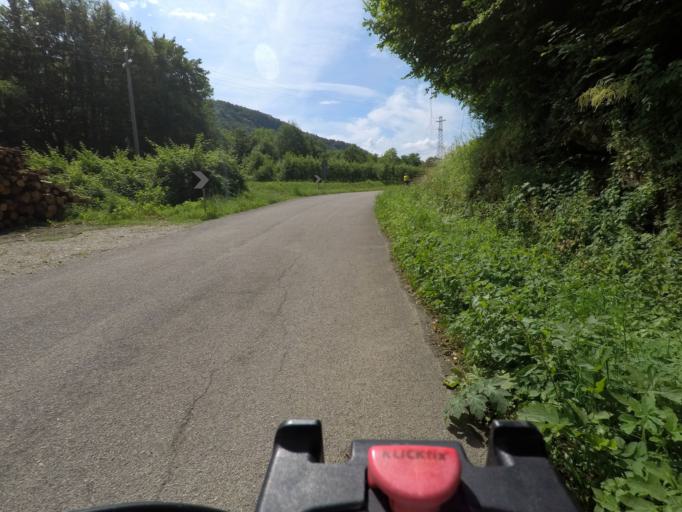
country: IT
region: Friuli Venezia Giulia
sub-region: Provincia di Udine
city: Pulfero
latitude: 46.1669
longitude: 13.4844
